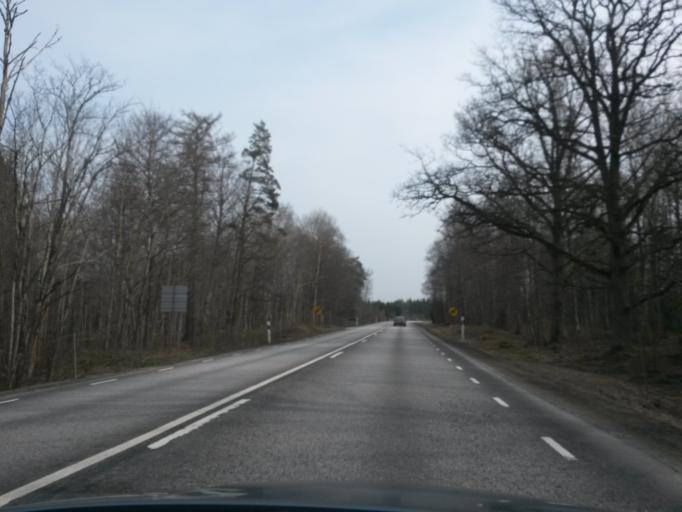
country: SE
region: Vaestra Goetaland
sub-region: Gullspangs Kommun
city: Anderstorp
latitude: 58.8783
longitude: 14.2675
